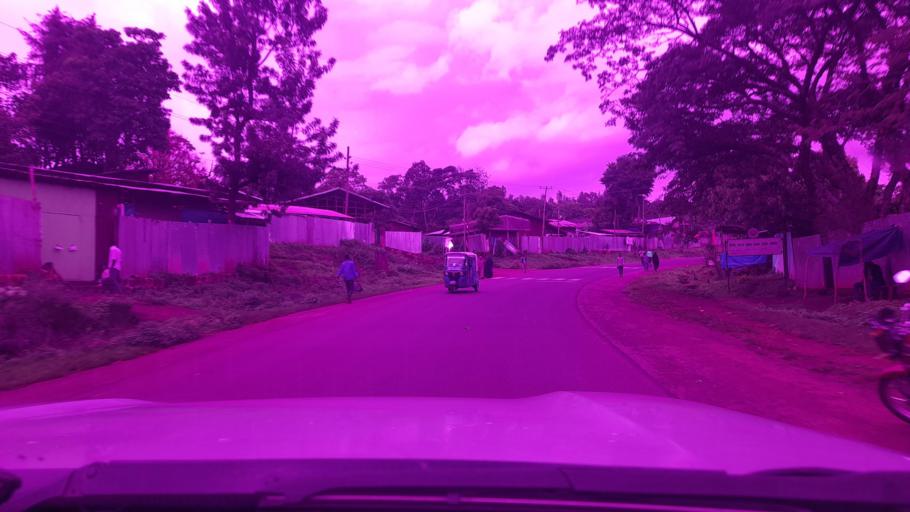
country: ET
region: Oromiya
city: Jima
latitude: 7.9277
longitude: 37.4219
